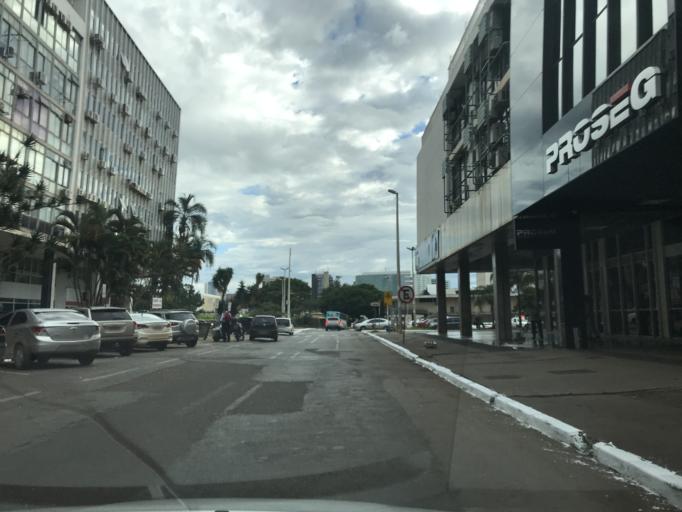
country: BR
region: Federal District
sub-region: Brasilia
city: Brasilia
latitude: -15.7973
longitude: -47.8881
